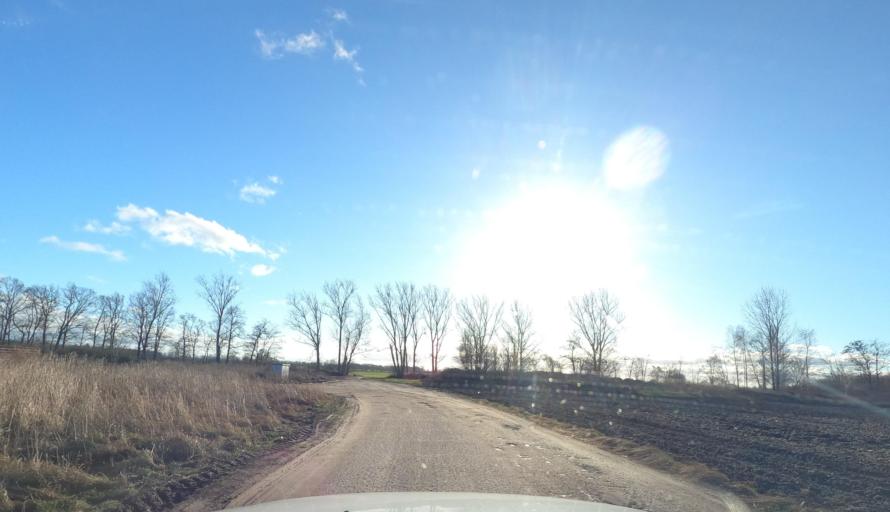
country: PL
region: West Pomeranian Voivodeship
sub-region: Powiat pyrzycki
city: Warnice
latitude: 53.2830
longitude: 14.9921
